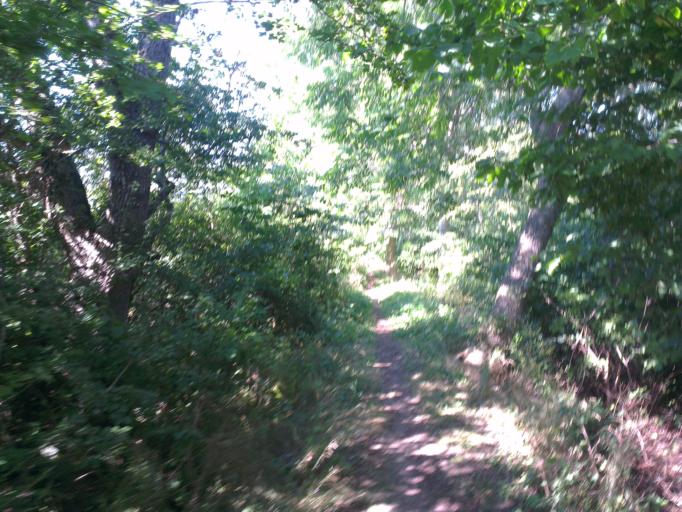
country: DK
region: Capital Region
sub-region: Frederikssund Kommune
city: Skibby
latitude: 55.7693
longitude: 12.0272
